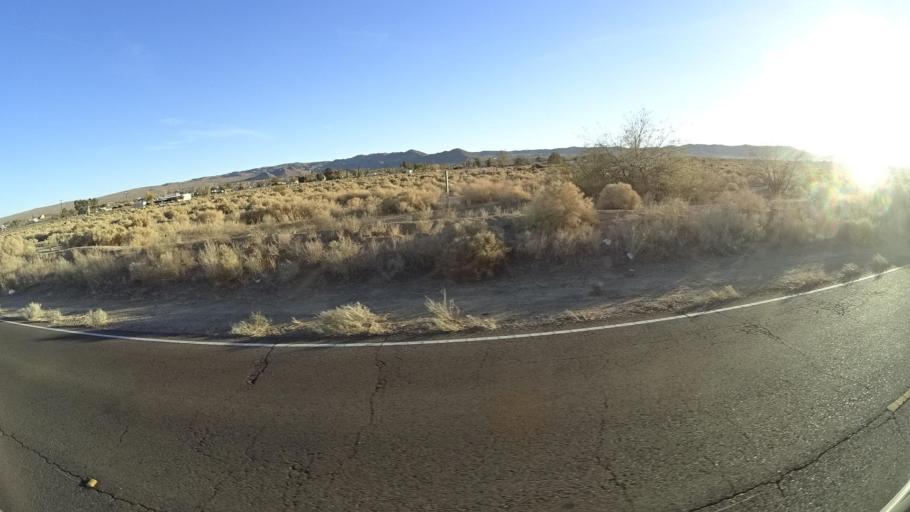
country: US
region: California
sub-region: Kern County
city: Ridgecrest
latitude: 35.6081
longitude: -117.6595
